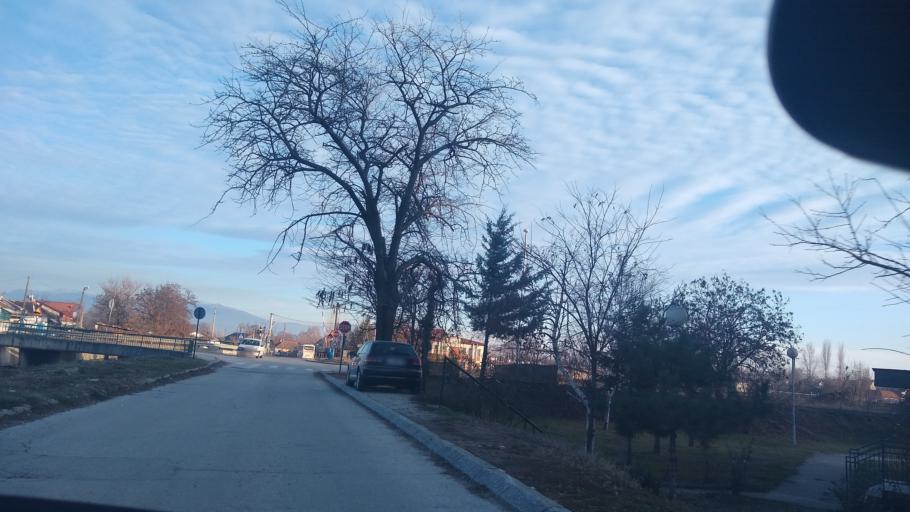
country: MK
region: Bitola
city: Bitola
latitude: 41.0295
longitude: 21.3467
